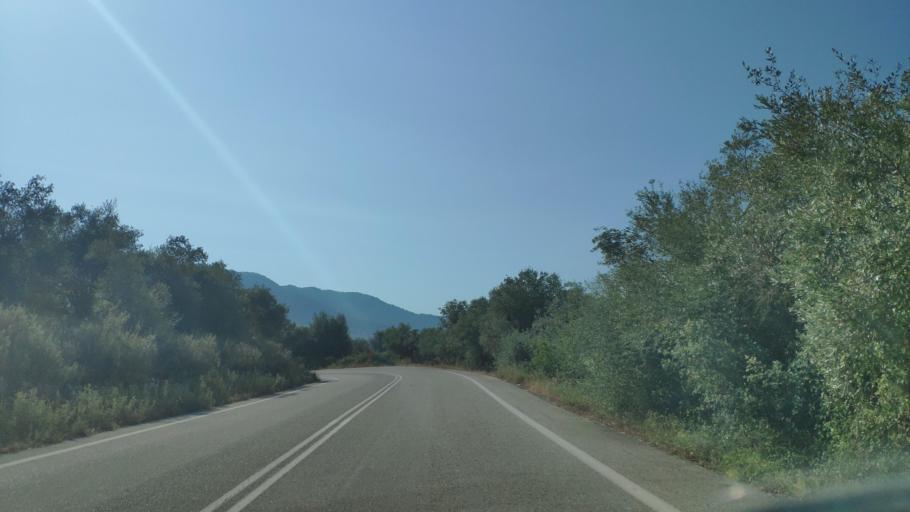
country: GR
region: West Greece
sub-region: Nomos Aitolias kai Akarnanias
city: Stanos
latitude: 38.7689
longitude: 21.1708
